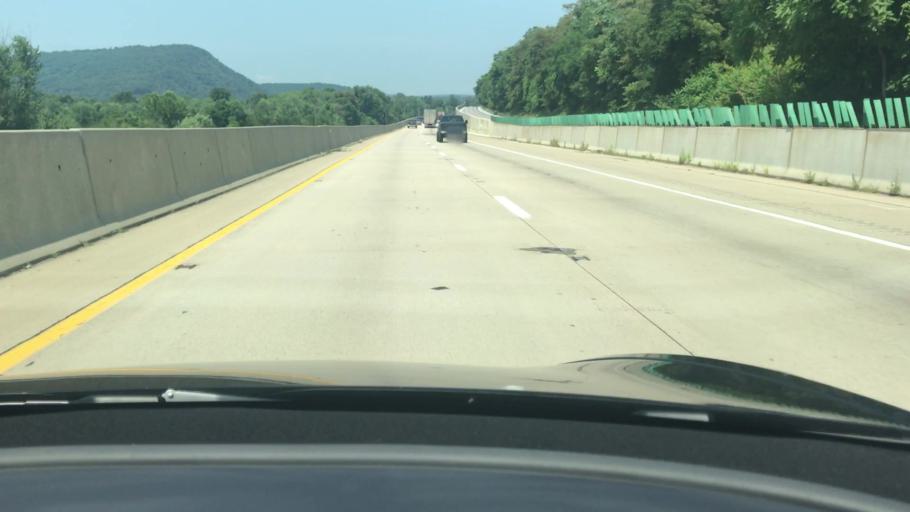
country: US
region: Pennsylvania
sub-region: Perry County
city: Duncannon
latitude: 40.3722
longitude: -76.9928
